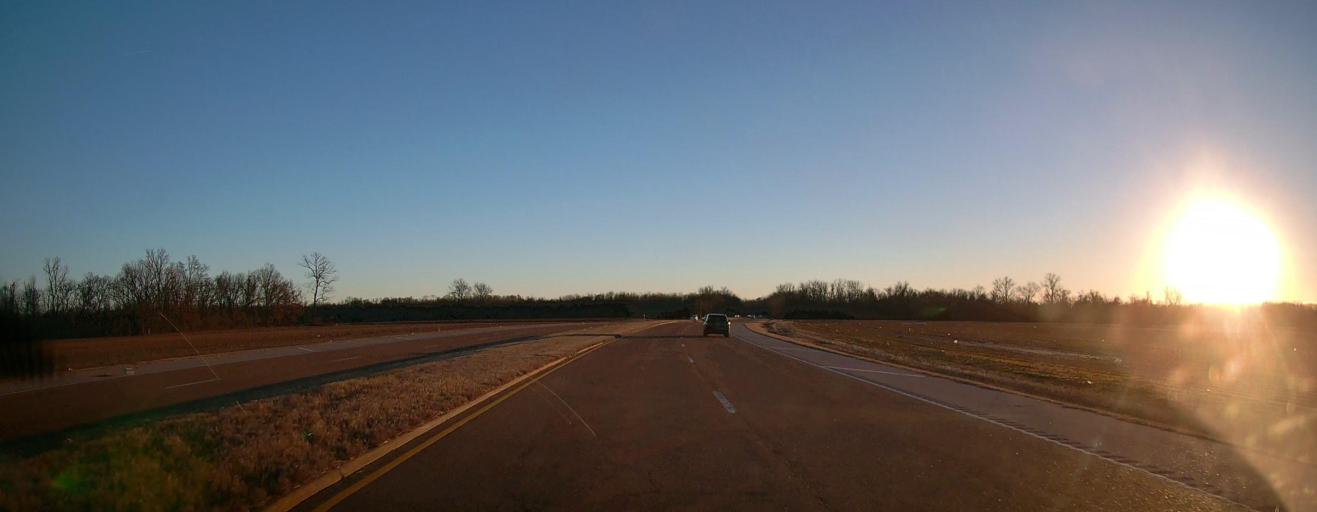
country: US
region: Tennessee
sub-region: Shelby County
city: Millington
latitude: 35.2872
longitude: -89.8820
